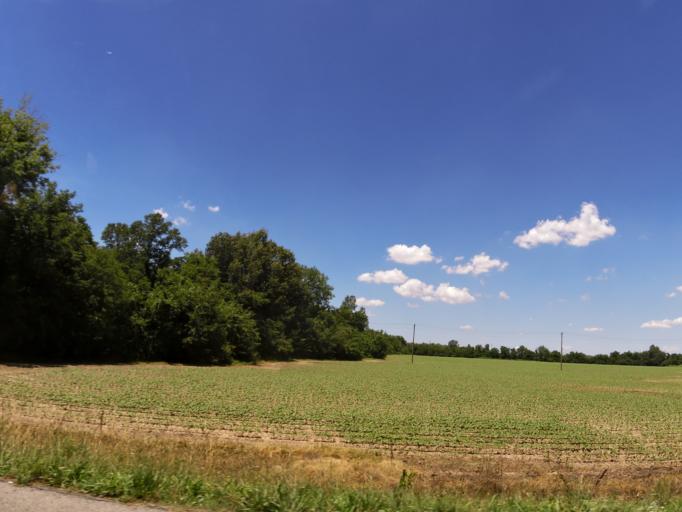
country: US
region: Missouri
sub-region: New Madrid County
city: New Madrid
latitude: 36.5851
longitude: -89.5483
